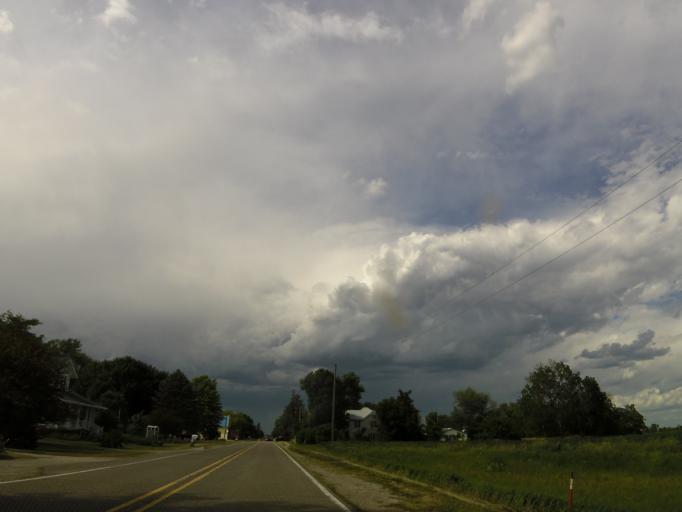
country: US
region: Iowa
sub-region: Henry County
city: Winfield
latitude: 41.1029
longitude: -91.5447
